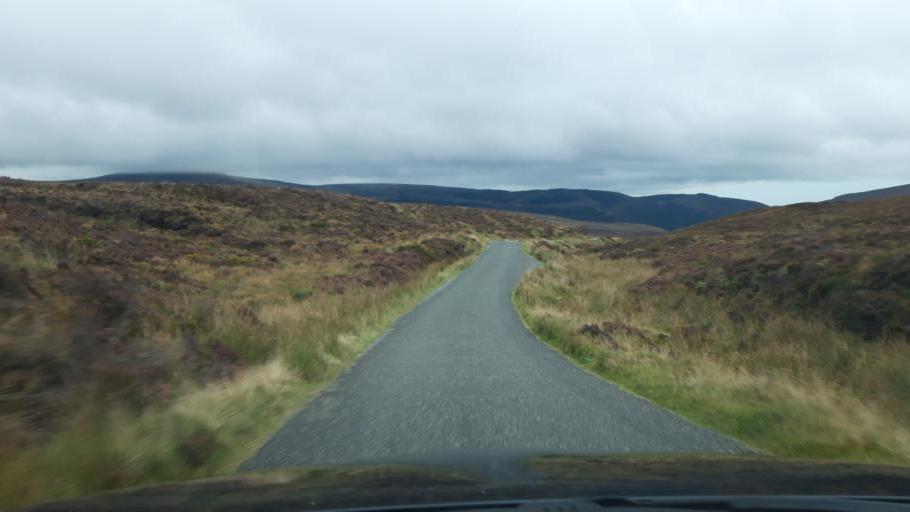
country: IE
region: Leinster
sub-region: Wicklow
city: Enniskerry
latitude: 53.1338
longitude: -6.3034
